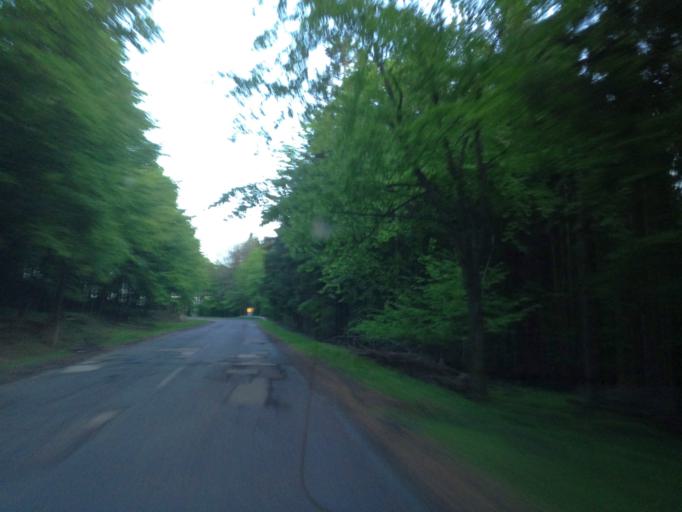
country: HU
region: Nograd
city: Batonyterenye
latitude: 47.8955
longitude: 19.8586
